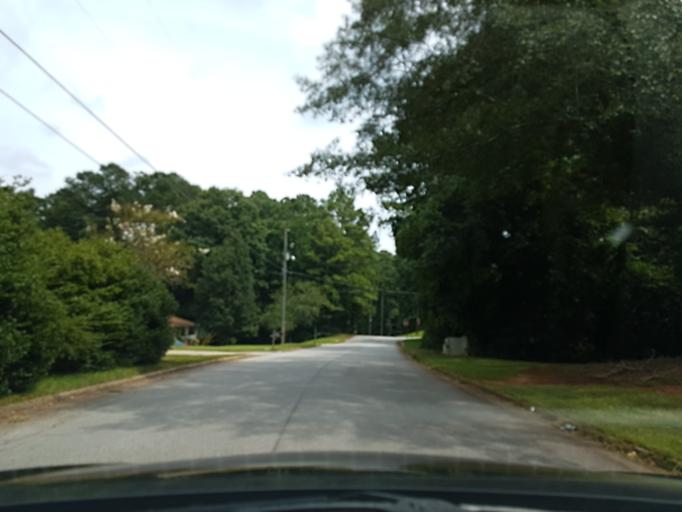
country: US
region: Georgia
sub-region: Douglas County
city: Douglasville
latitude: 33.6929
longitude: -84.7143
